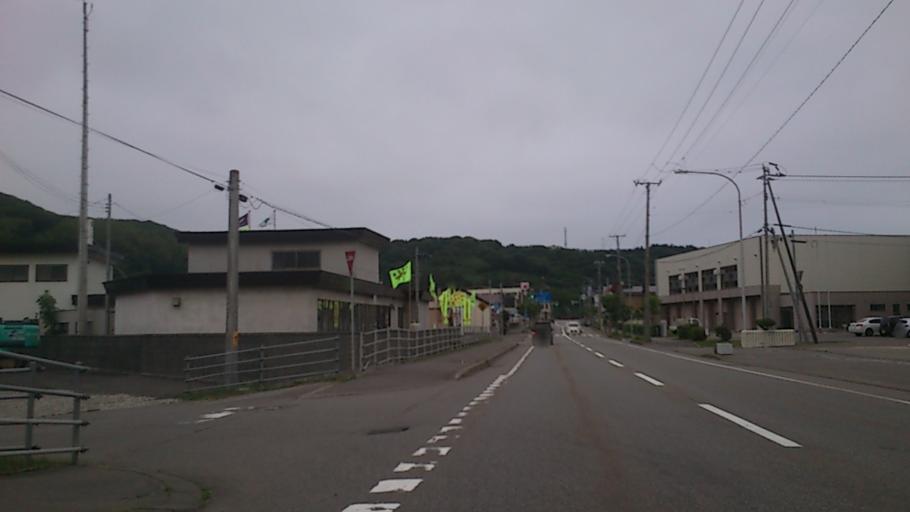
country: JP
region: Hokkaido
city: Kamiiso
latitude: 41.9726
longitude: 140.1395
